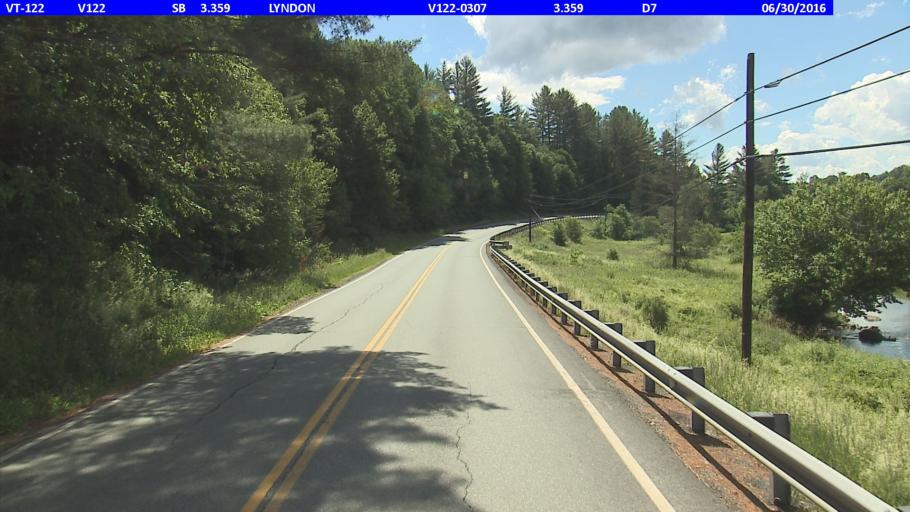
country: US
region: Vermont
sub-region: Caledonia County
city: Lyndonville
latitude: 44.5716
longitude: -72.0469
